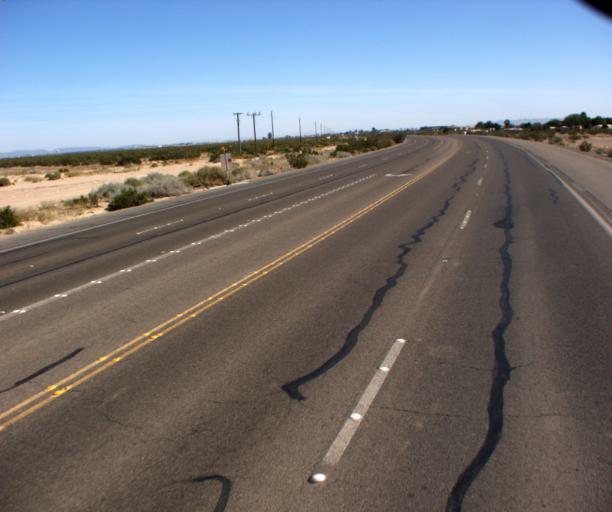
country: US
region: Arizona
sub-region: Yuma County
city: Somerton
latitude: 32.5979
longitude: -114.6665
